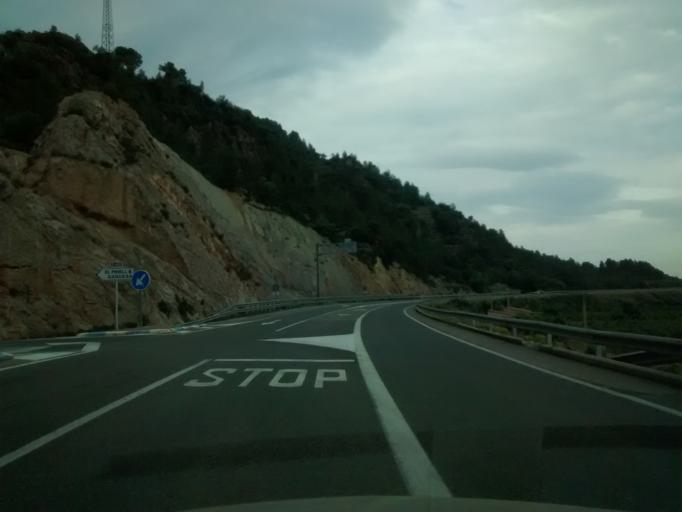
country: ES
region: Catalonia
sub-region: Provincia de Tarragona
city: Benifallet
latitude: 40.9805
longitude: 0.5168
